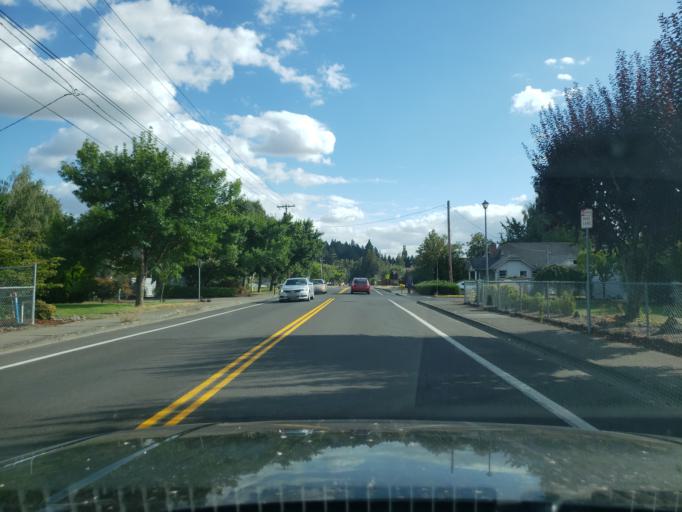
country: US
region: Oregon
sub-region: Yamhill County
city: McMinnville
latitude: 45.1996
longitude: -123.2191
